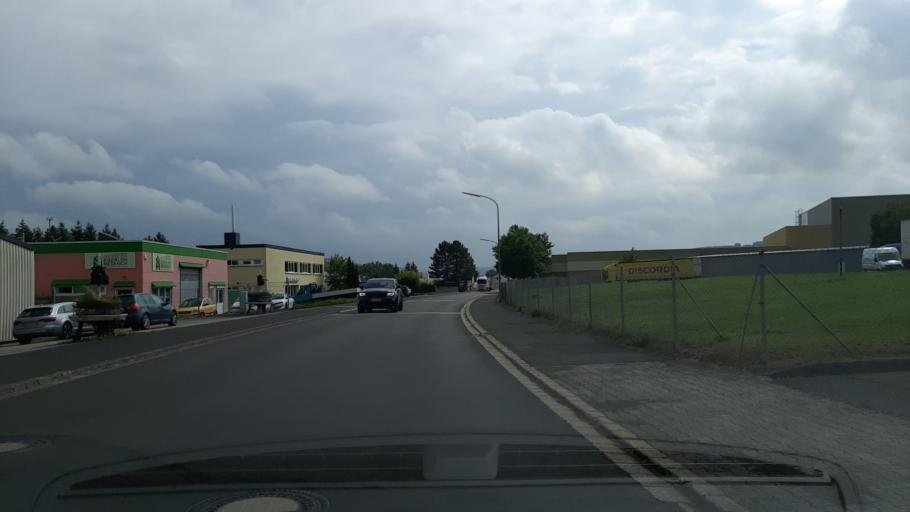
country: DE
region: Rheinland-Pfalz
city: Briedel
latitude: 50.0311
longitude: 7.1607
